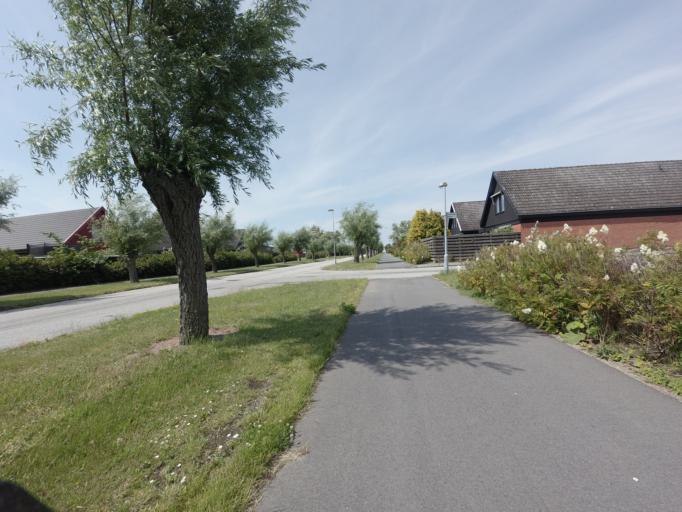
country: SE
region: Skane
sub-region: Malmo
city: Bunkeflostrand
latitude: 55.5492
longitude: 12.9152
